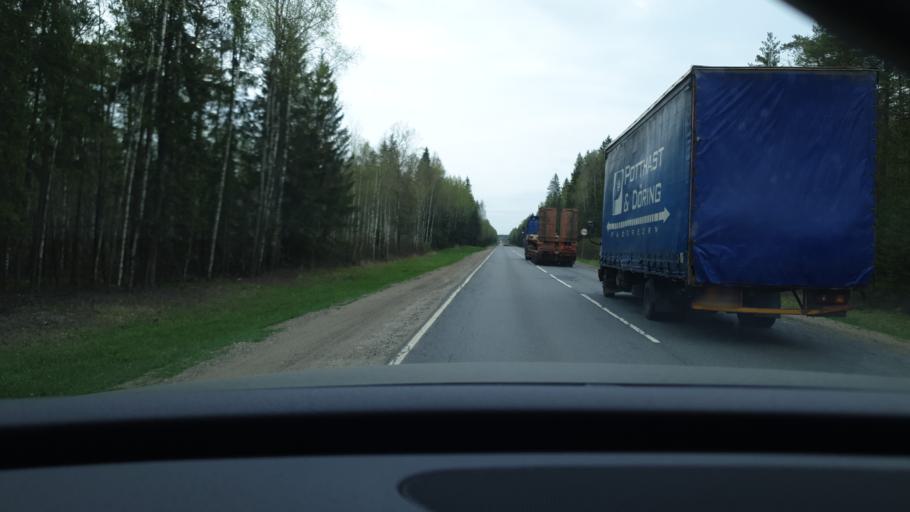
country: RU
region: Moskovskaya
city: Rumyantsevo
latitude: 56.1229
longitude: 36.5743
